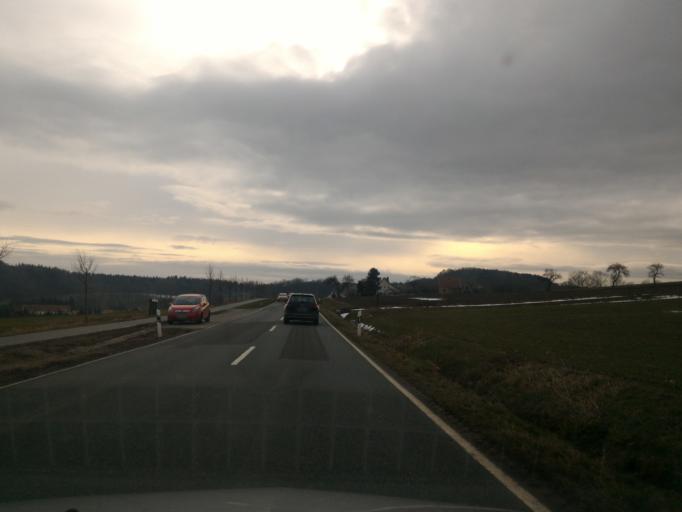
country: DE
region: Saxony
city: Leutersdorf
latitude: 50.9391
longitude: 14.6691
